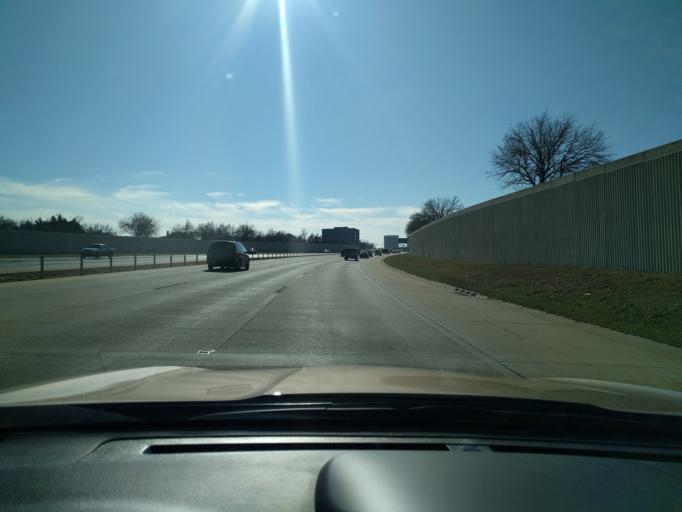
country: US
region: Oklahoma
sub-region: Oklahoma County
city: Nichols Hills
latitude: 35.5428
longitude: -97.5757
